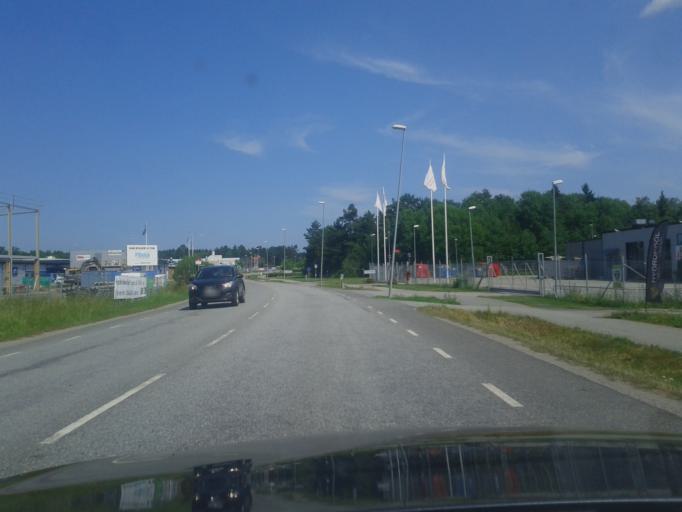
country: SE
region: Stockholm
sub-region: Taby Kommun
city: Taby
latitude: 59.4659
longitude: 18.1262
